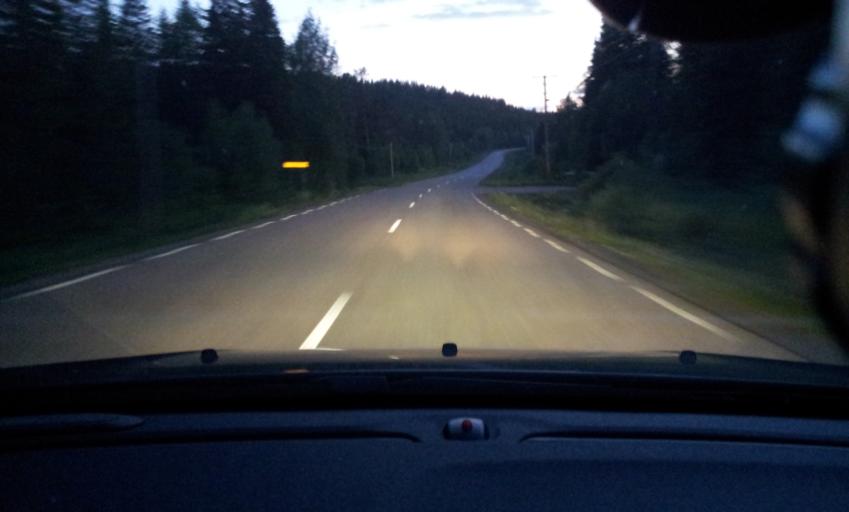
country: SE
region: Jaemtland
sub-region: OEstersunds Kommun
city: Brunflo
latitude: 62.6556
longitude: 14.8831
